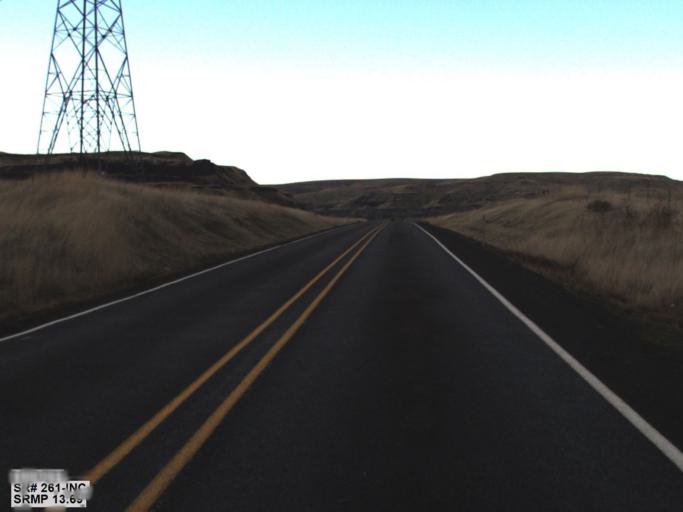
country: US
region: Washington
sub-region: Walla Walla County
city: Waitsburg
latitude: 46.5740
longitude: -118.2058
